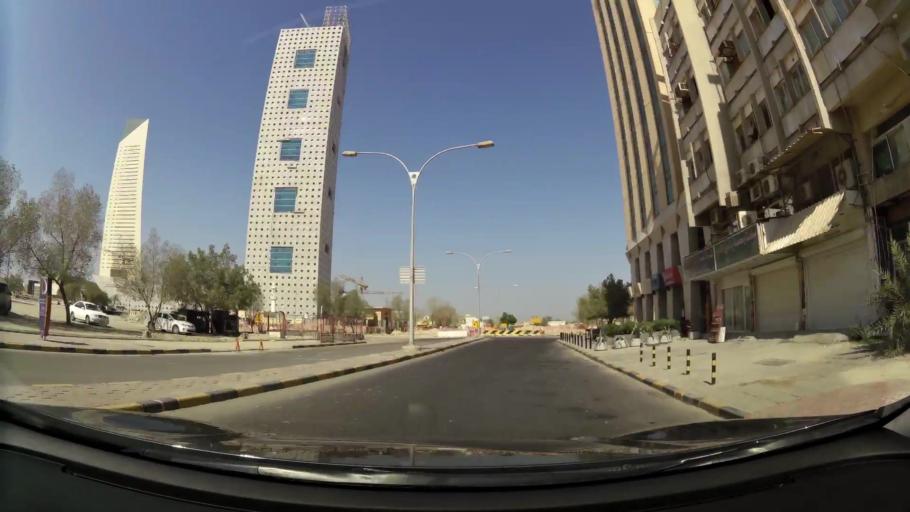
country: KW
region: Al Asimah
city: Kuwait City
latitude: 29.3810
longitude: 47.9826
